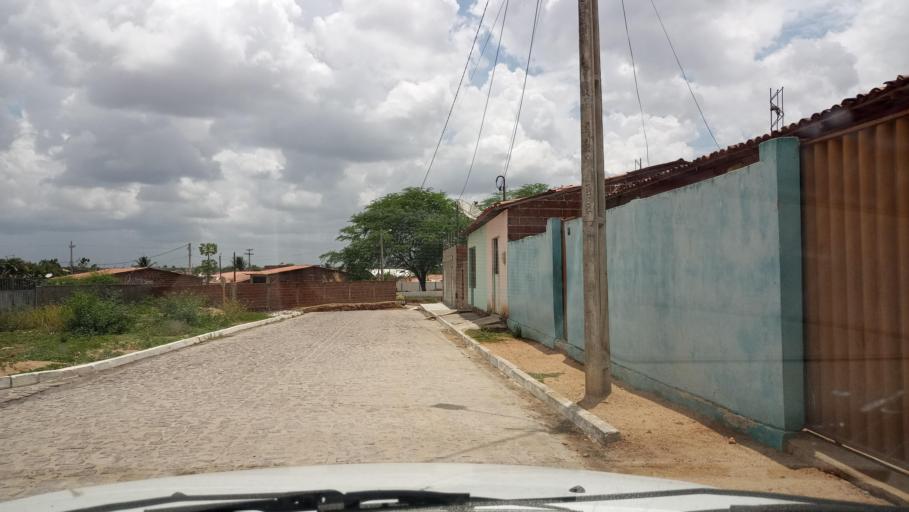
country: BR
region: Rio Grande do Norte
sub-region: Tangara
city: Tangara
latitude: -6.1015
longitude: -35.7128
